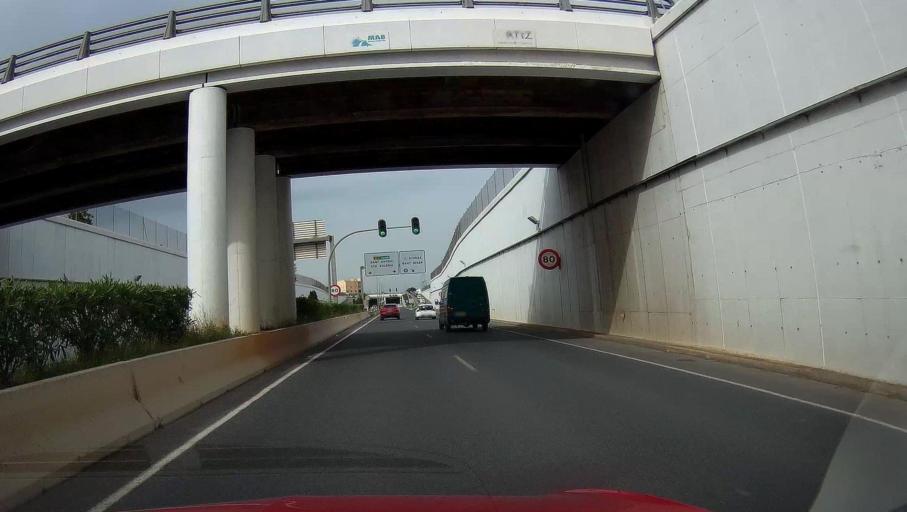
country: ES
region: Balearic Islands
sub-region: Illes Balears
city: Ibiza
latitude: 38.9003
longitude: 1.4048
